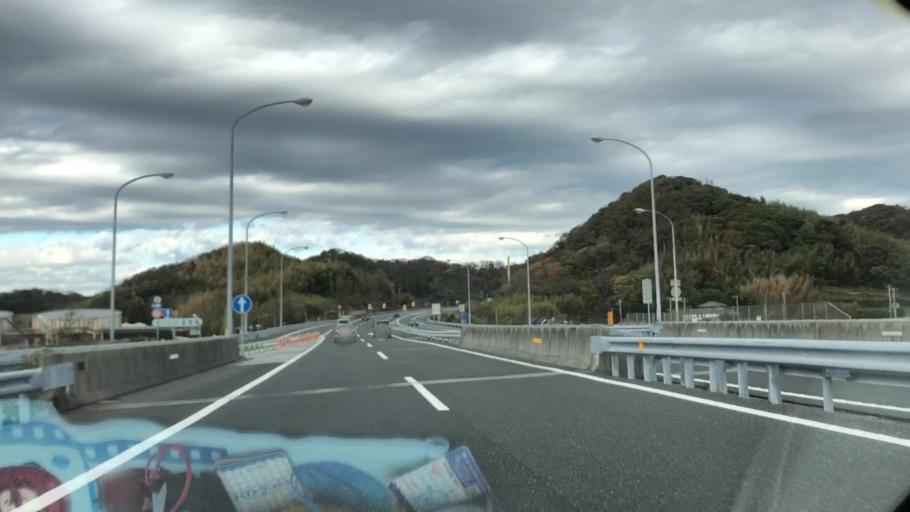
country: JP
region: Chiba
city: Tateyama
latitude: 35.1002
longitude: 139.8572
